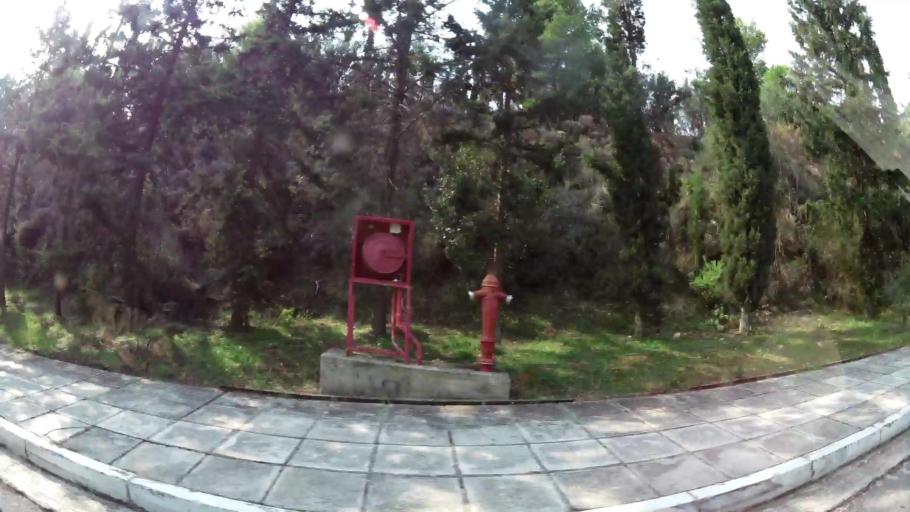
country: GR
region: Attica
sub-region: Nomarchia Athinas
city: Psychiko
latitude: 38.0036
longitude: 23.7594
